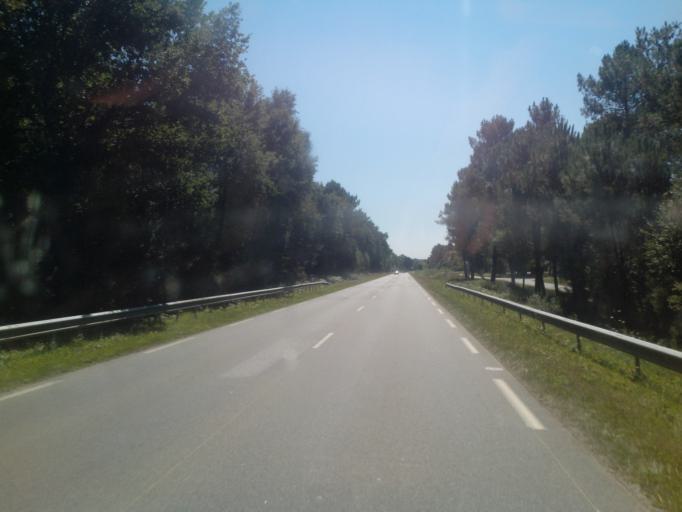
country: FR
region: Brittany
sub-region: Departement du Morbihan
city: Molac
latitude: 47.7419
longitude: -2.4377
